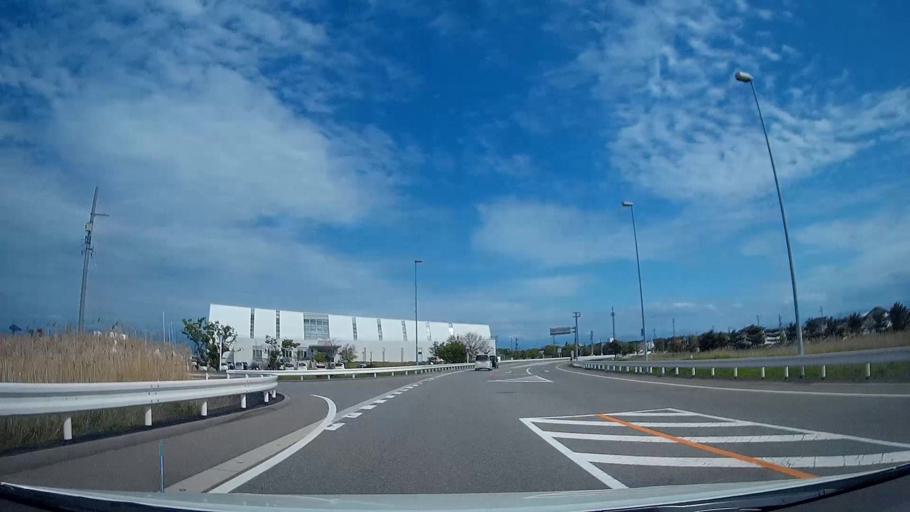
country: JP
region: Toyama
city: Kuragaki-kosugi
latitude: 36.7722
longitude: 137.1328
